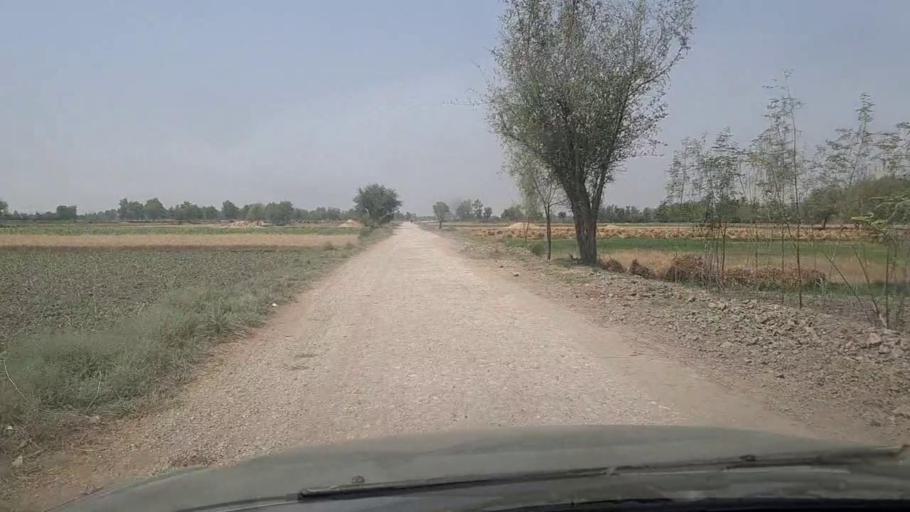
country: PK
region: Sindh
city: Adilpur
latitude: 27.9333
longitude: 69.2656
